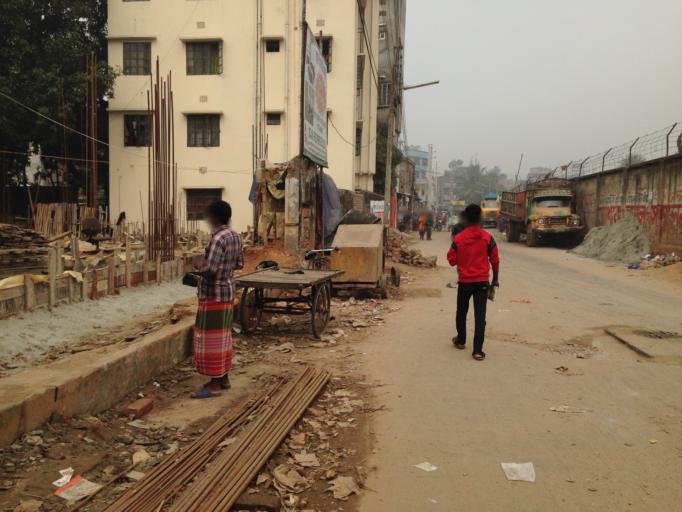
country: BD
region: Dhaka
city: Azimpur
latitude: 23.7945
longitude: 90.3433
